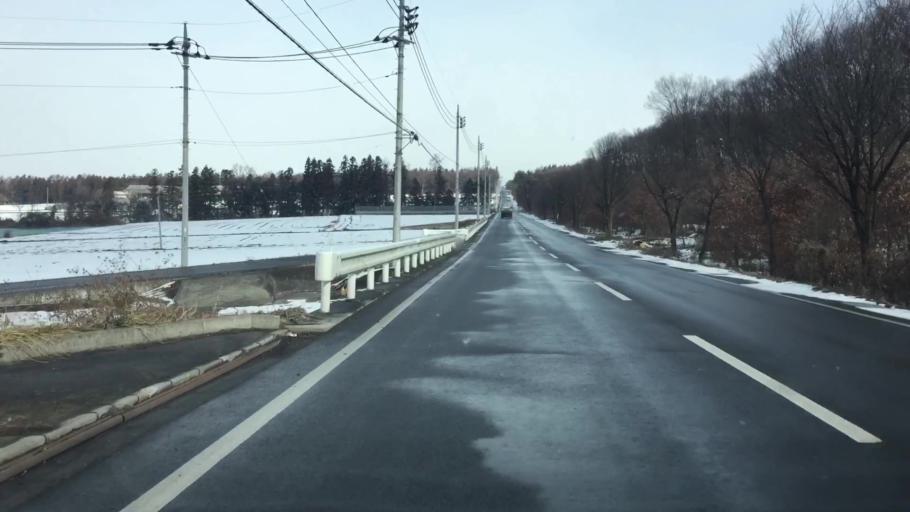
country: JP
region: Gunma
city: Numata
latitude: 36.6152
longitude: 139.0818
